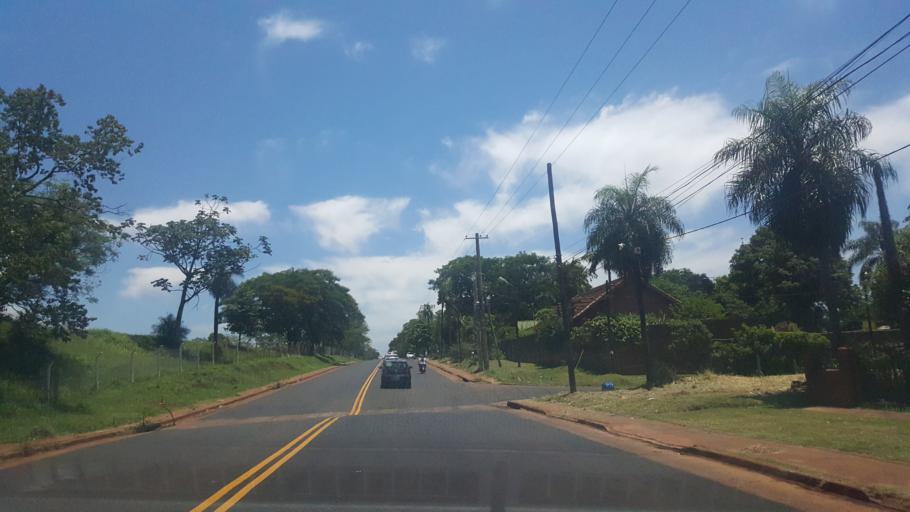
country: AR
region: Misiones
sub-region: Departamento de Capital
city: Posadas
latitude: -27.3617
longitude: -55.9202
